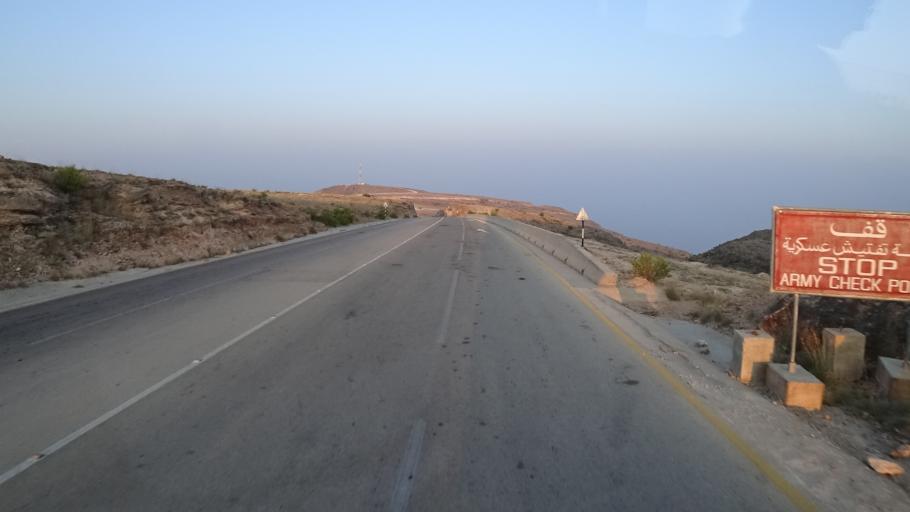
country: OM
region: Zufar
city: Salalah
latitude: 16.8262
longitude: 53.6524
